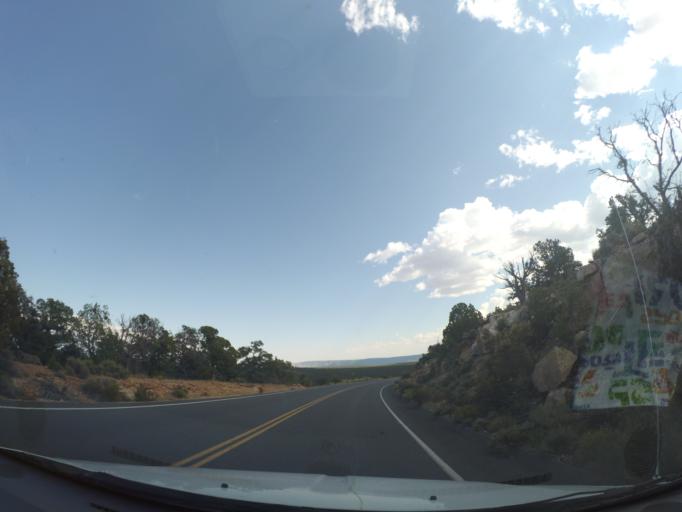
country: US
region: Arizona
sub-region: Coconino County
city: Grand Canyon
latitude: 36.0175
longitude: -111.8089
